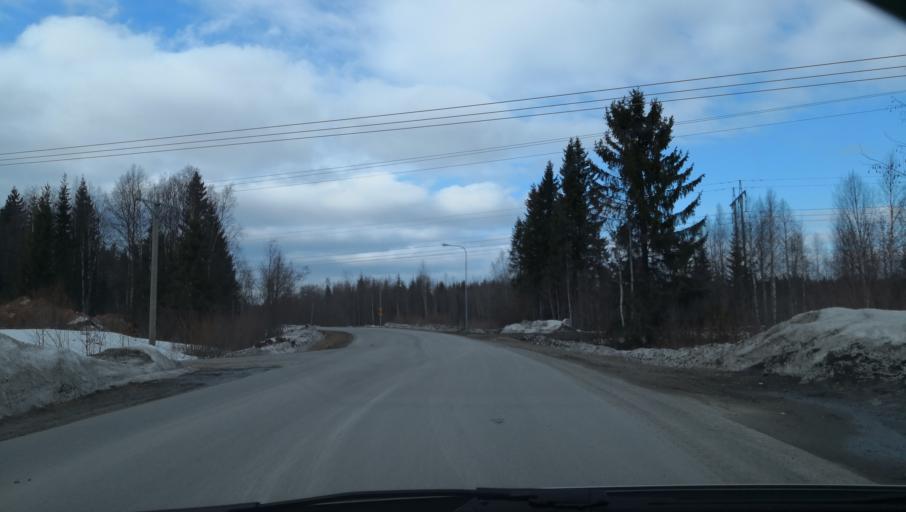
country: SE
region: Vaesterbotten
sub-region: Vannas Kommun
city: Vaennaes
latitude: 63.9171
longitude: 19.7429
